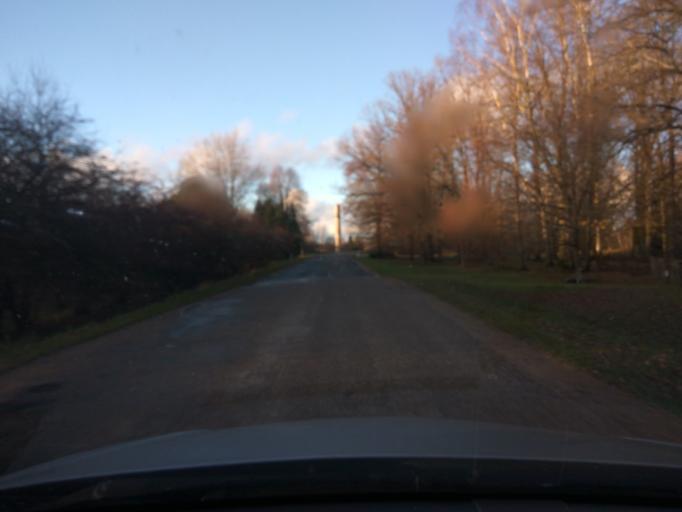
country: LV
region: Aizpute
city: Aizpute
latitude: 56.8311
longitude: 21.7729
